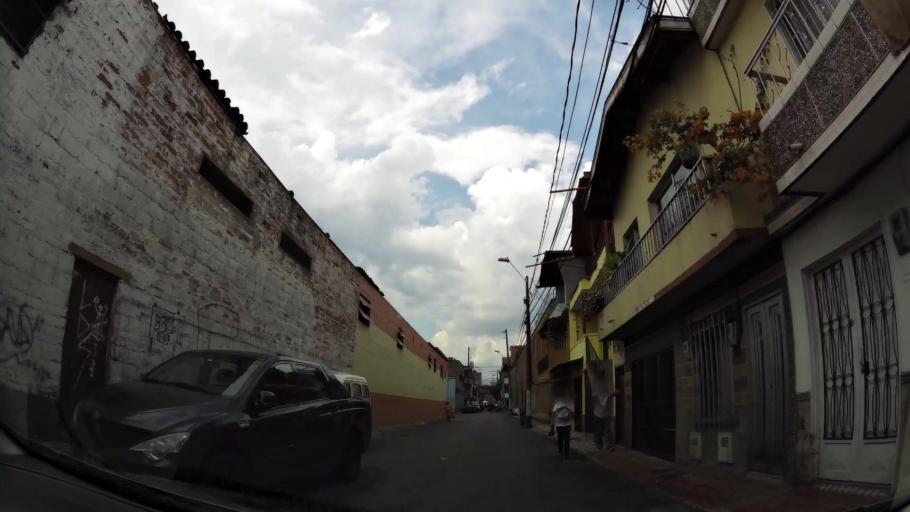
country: CO
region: Antioquia
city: Itagui
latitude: 6.1930
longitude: -75.5881
